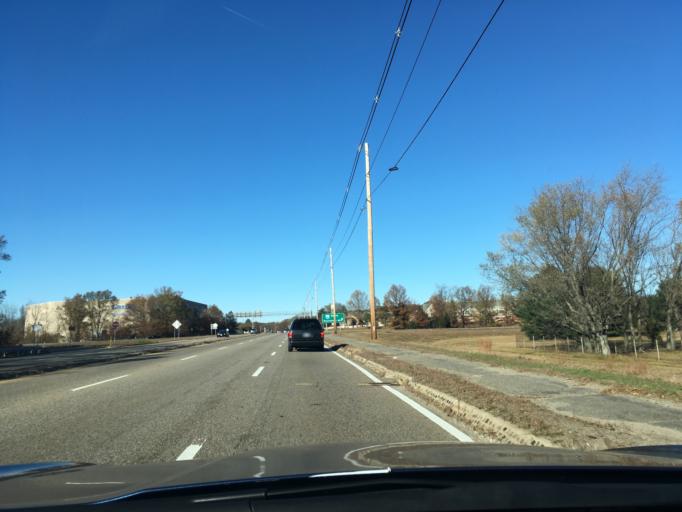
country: US
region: Massachusetts
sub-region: Bristol County
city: North Seekonk
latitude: 41.9030
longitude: -71.3560
